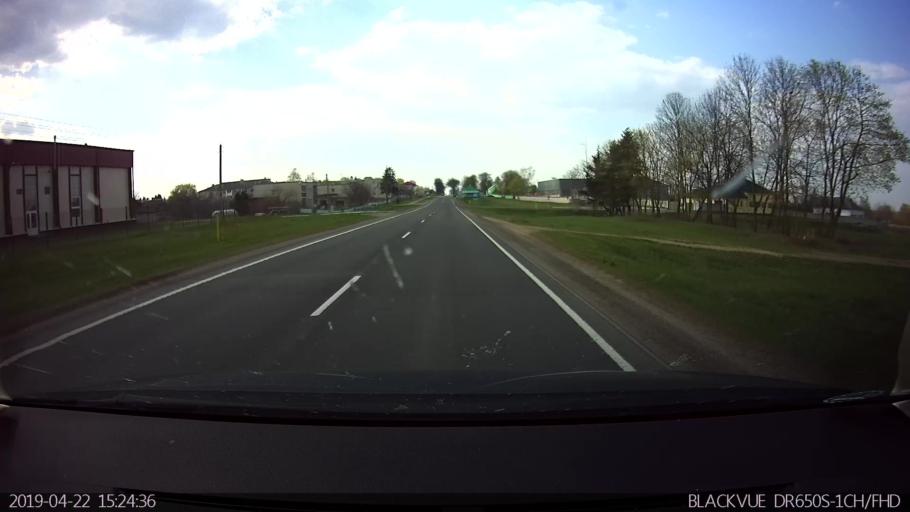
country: BY
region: Brest
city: Vysokaye
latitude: 52.3615
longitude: 23.4058
